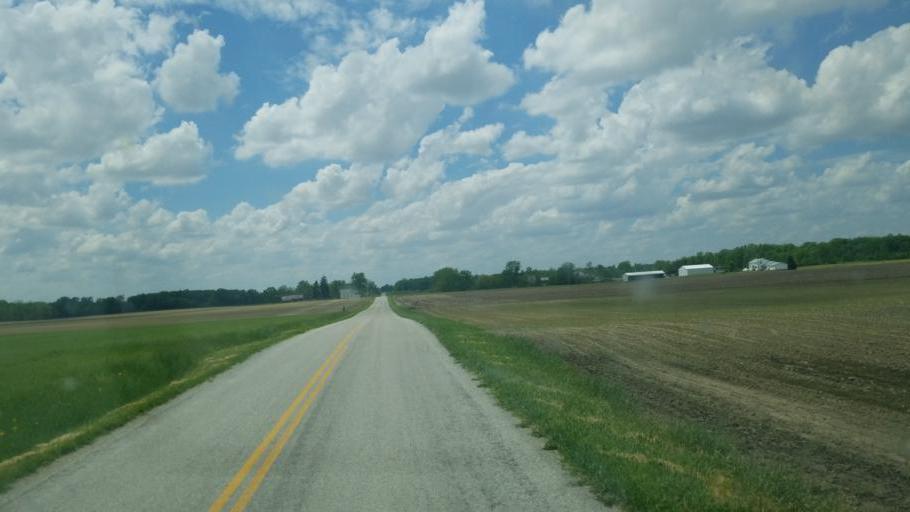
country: US
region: Ohio
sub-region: Crawford County
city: Galion
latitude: 40.6899
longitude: -82.9129
